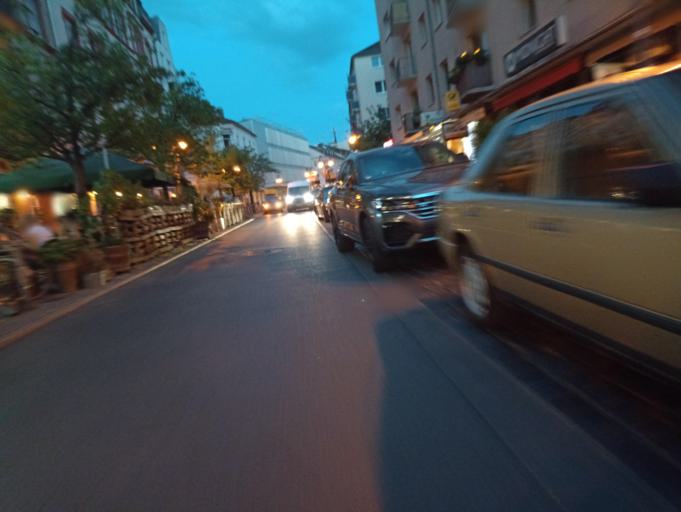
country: DE
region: Hesse
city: Niederrad
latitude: 50.1238
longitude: 8.6414
